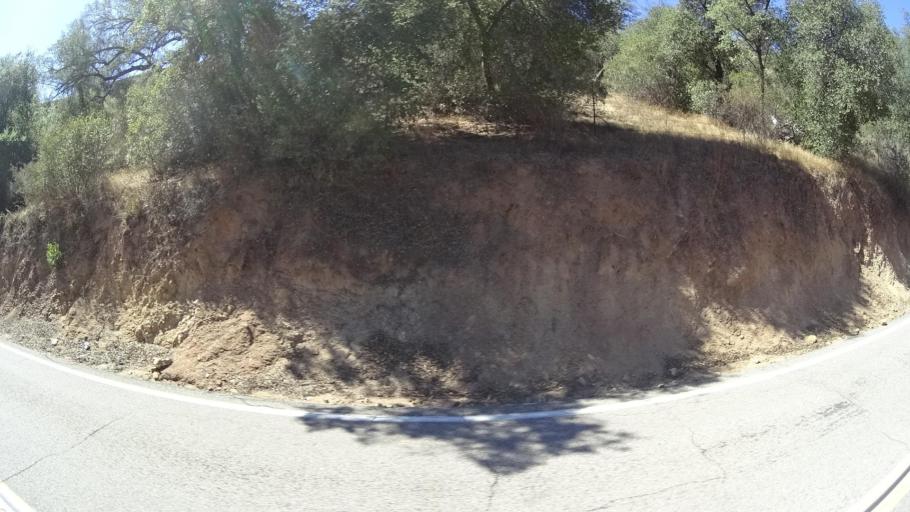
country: US
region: California
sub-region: San Diego County
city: Alpine
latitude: 32.7089
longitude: -116.7387
